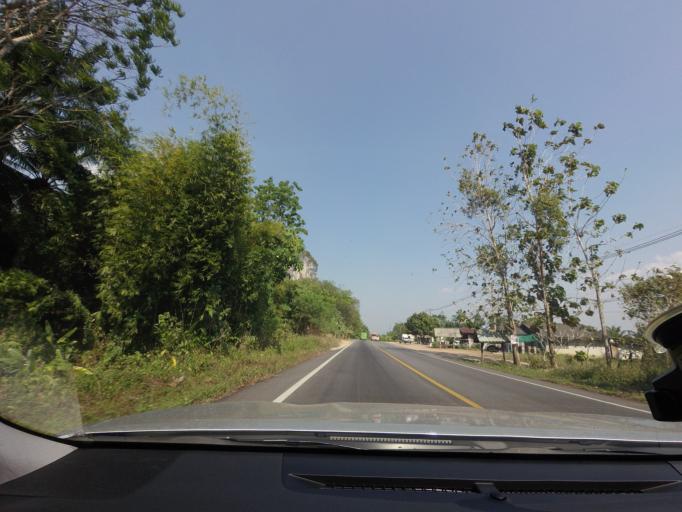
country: TH
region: Krabi
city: Plai Phraya
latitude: 8.5557
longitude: 98.7867
